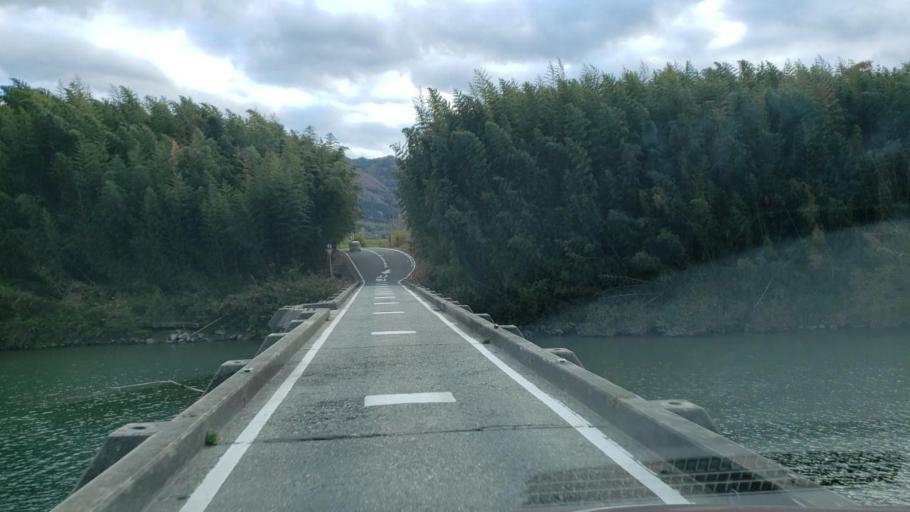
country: JP
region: Tokushima
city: Wakimachi
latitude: 34.0645
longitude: 134.1432
